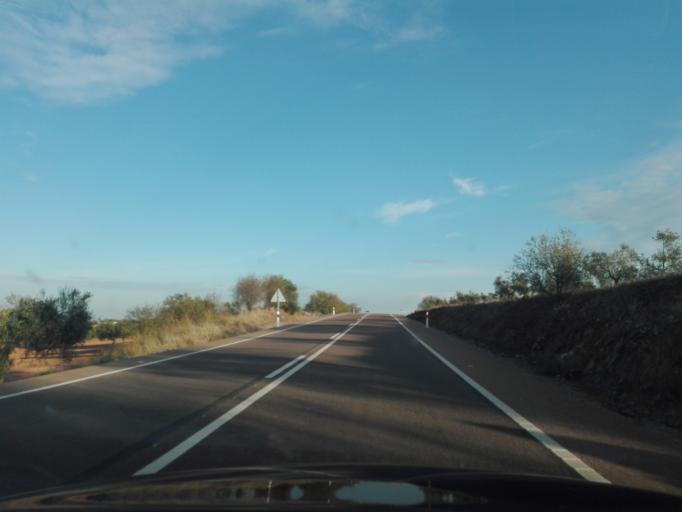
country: ES
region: Extremadura
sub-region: Provincia de Badajoz
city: Usagre
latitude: 38.3520
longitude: -6.1960
